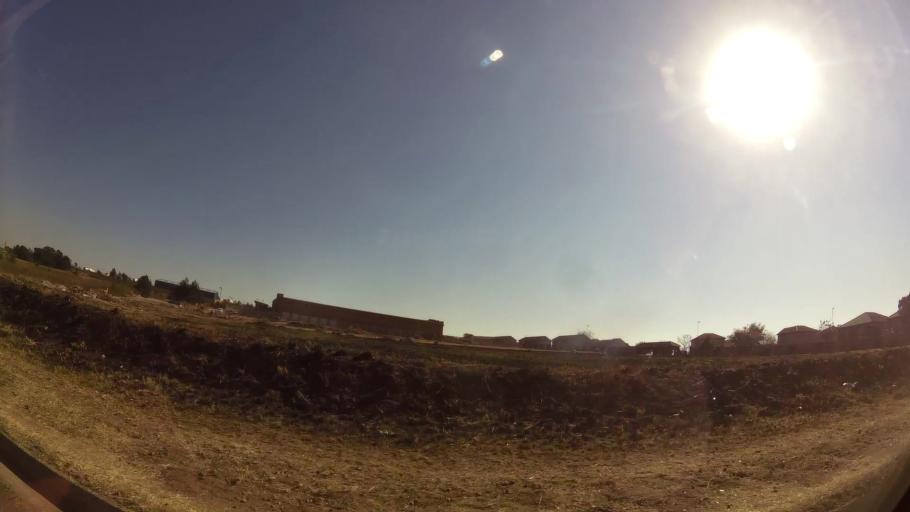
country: ZA
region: Gauteng
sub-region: Ekurhuleni Metropolitan Municipality
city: Germiston
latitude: -26.2507
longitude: 28.1127
